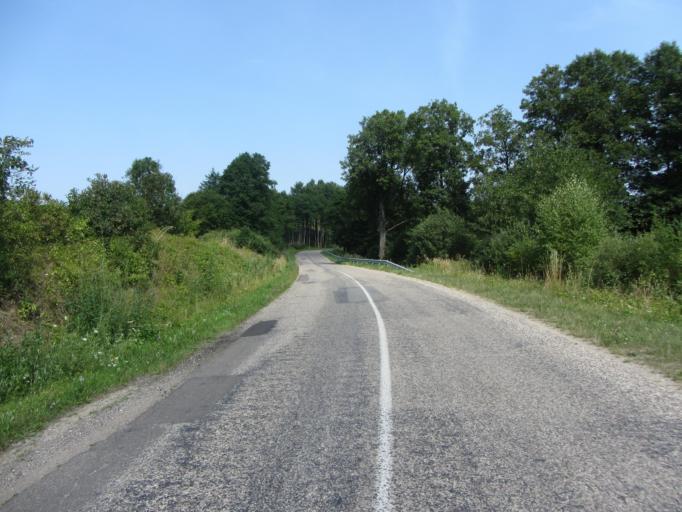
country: LT
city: Veisiejai
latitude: 54.0988
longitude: 23.6754
